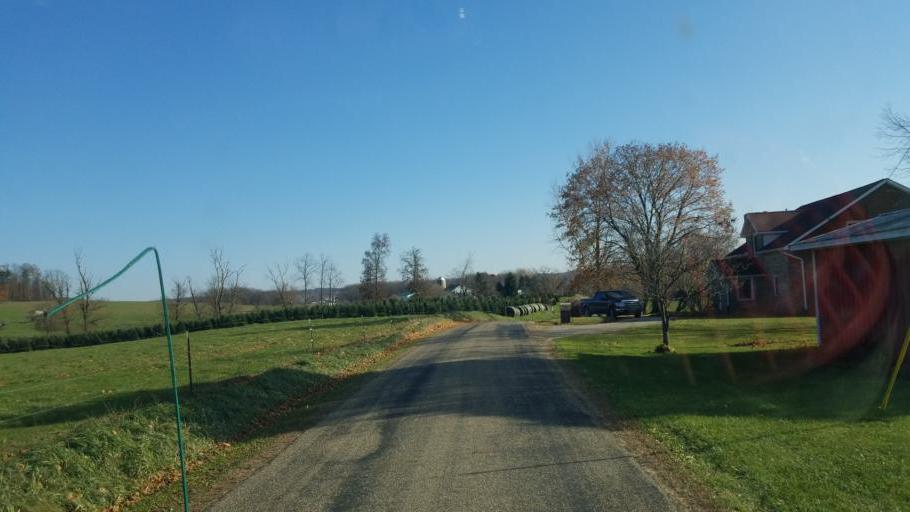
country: US
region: Ohio
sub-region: Richland County
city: Lexington
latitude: 40.6270
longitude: -82.6033
